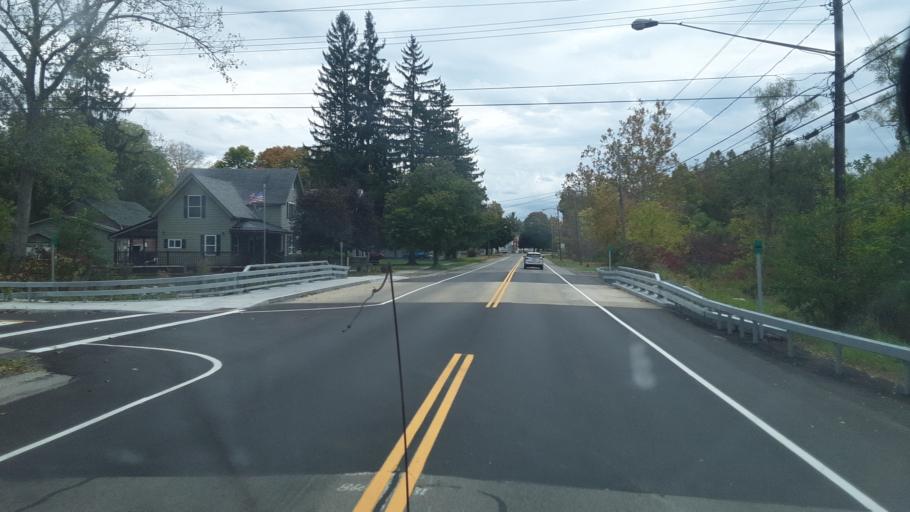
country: US
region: New York
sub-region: Allegany County
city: Belmont
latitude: 42.2241
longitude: -78.0271
